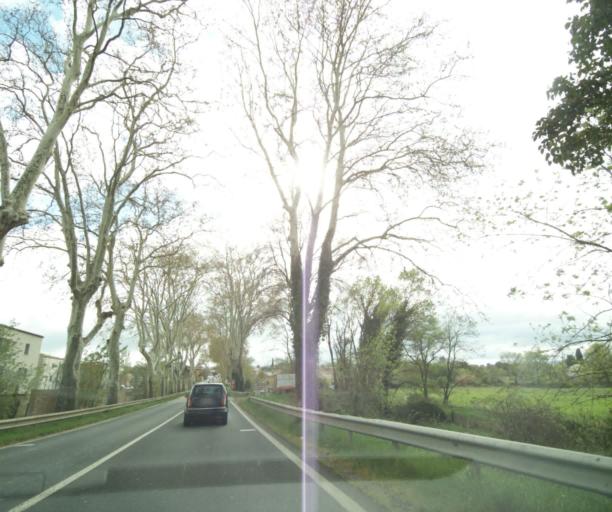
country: FR
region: Languedoc-Roussillon
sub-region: Departement de l'Herault
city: Fabregues
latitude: 43.5523
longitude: 3.7852
